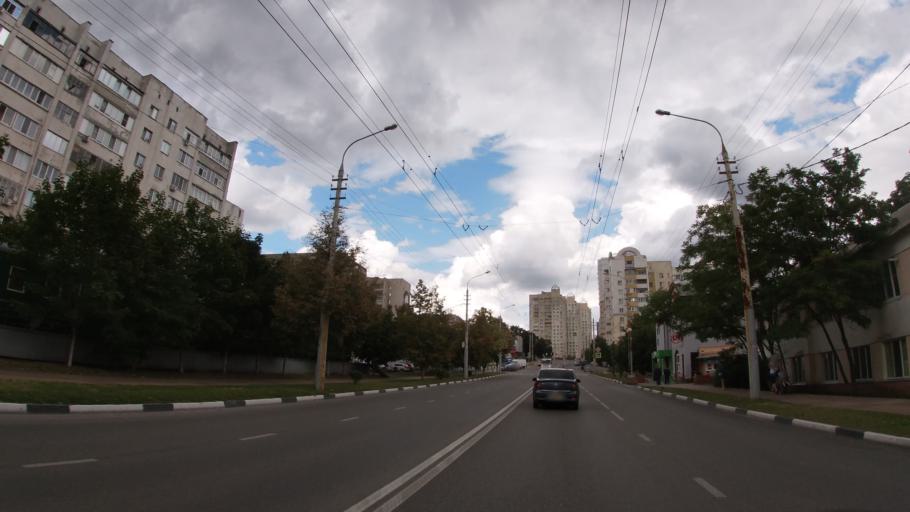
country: RU
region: Belgorod
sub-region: Belgorodskiy Rayon
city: Belgorod
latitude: 50.5973
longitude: 36.6065
